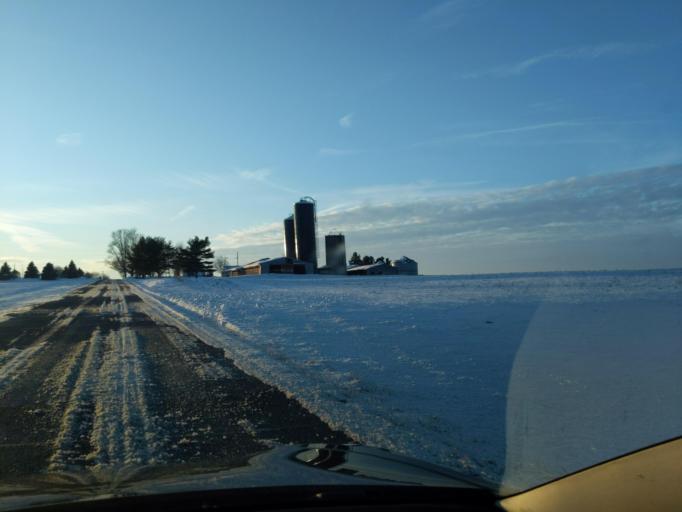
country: US
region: Michigan
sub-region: Ingham County
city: Webberville
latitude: 42.5695
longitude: -84.1858
